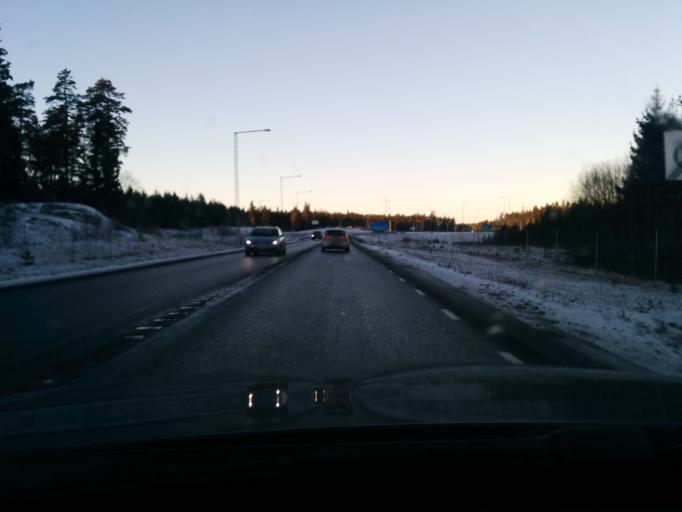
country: SE
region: Stockholm
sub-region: Vallentuna Kommun
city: Vallentuna
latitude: 59.4859
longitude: 18.1126
